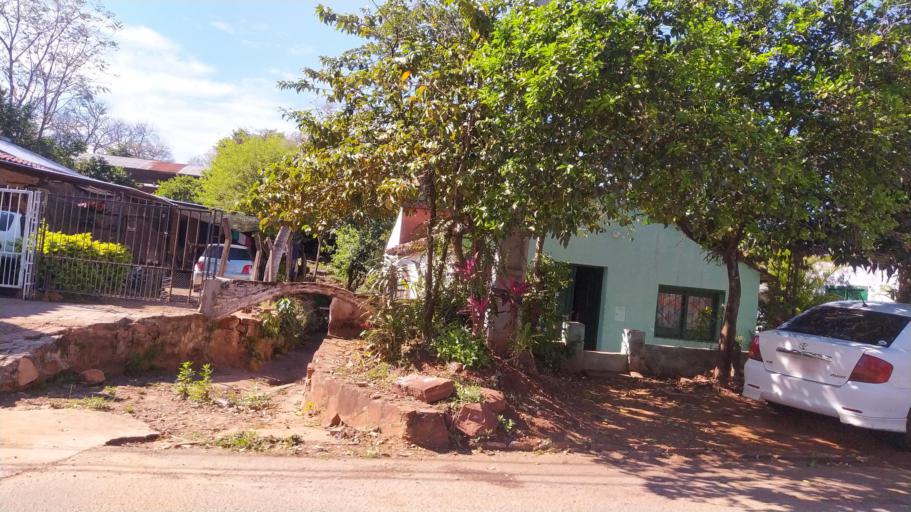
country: PY
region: Misiones
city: San Juan Bautista
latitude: -26.6710
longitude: -57.1371
